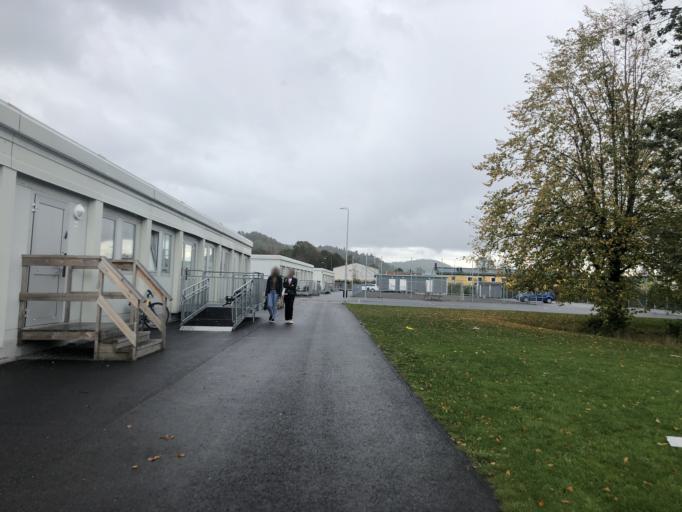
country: SE
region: Vaestra Goetaland
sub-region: Molndal
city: Moelndal
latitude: 57.6513
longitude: 12.0262
